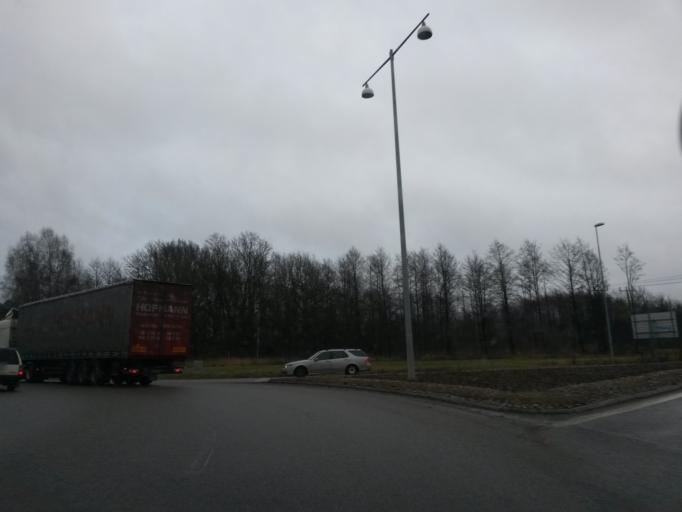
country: SE
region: Vaestra Goetaland
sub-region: Uddevalla Kommun
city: Uddevalla
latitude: 58.3524
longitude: 11.8692
